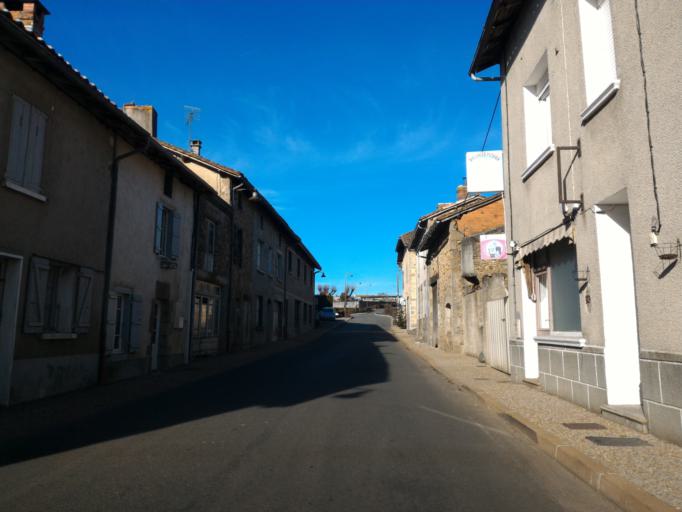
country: FR
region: Poitou-Charentes
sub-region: Departement de la Charente
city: Etagnac
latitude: 45.9506
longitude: 0.7834
